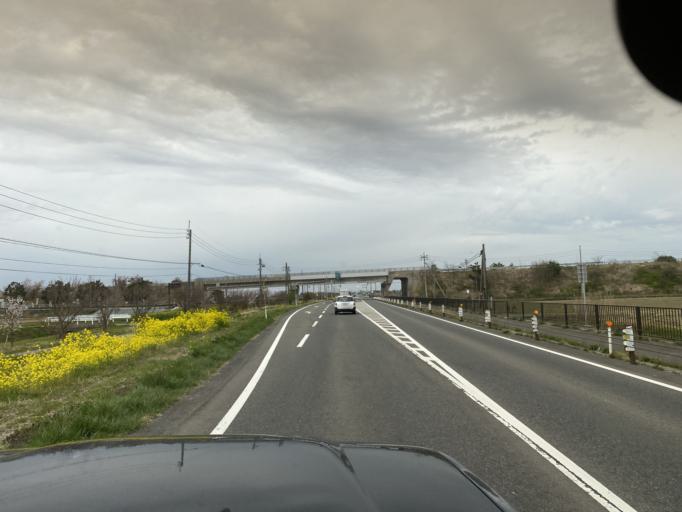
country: JP
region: Niigata
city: Niitsu-honcho
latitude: 37.8192
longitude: 139.0993
